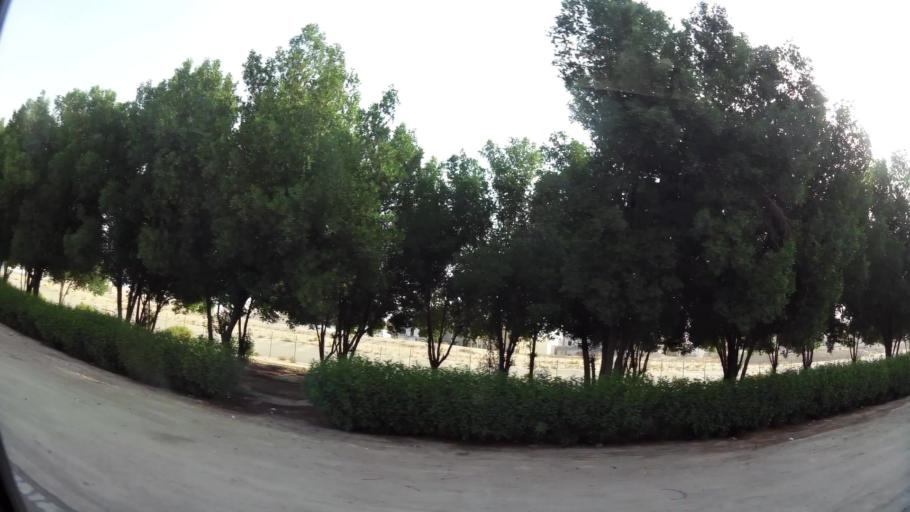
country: KW
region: Al Asimah
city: Ar Rabiyah
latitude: 29.3248
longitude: 47.8006
